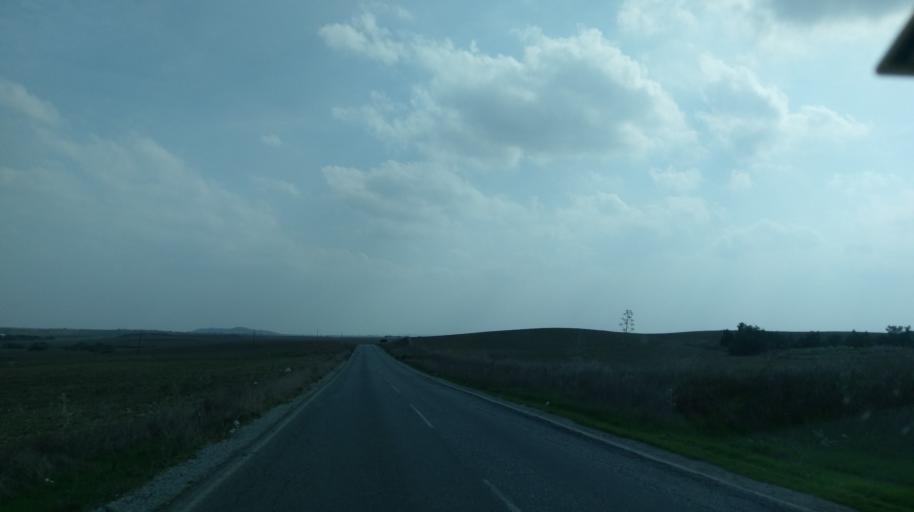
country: CY
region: Keryneia
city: Lapithos
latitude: 35.2523
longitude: 33.1459
